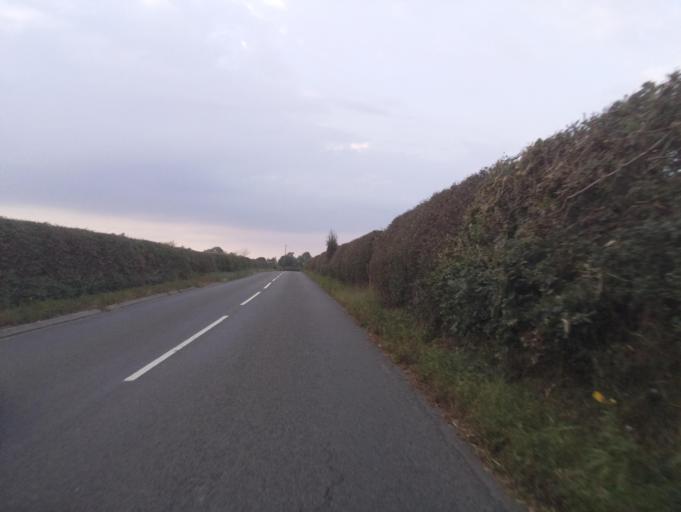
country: GB
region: England
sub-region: Lincolnshire
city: Skellingthorpe
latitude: 53.1382
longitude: -0.6452
